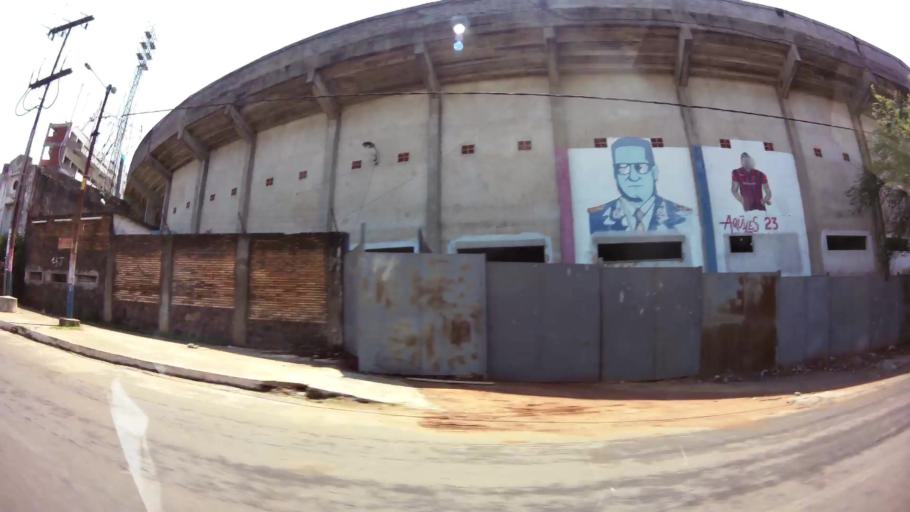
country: PY
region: Asuncion
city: Asuncion
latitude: -25.3006
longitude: -57.6382
